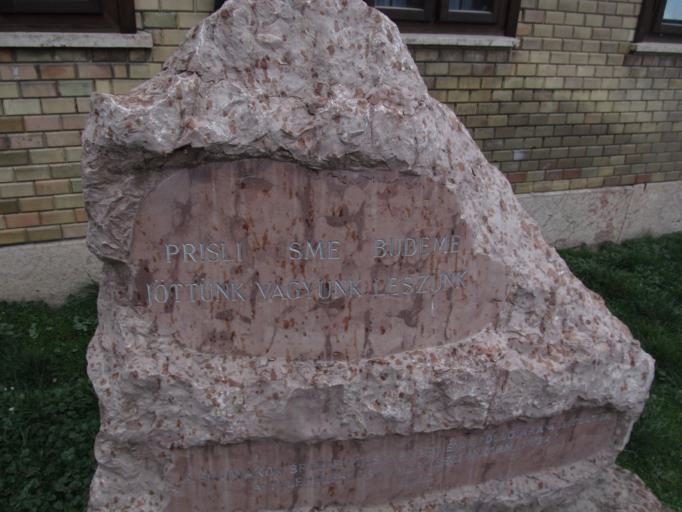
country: HU
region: Komarom-Esztergom
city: Tardos
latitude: 47.6629
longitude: 18.4472
